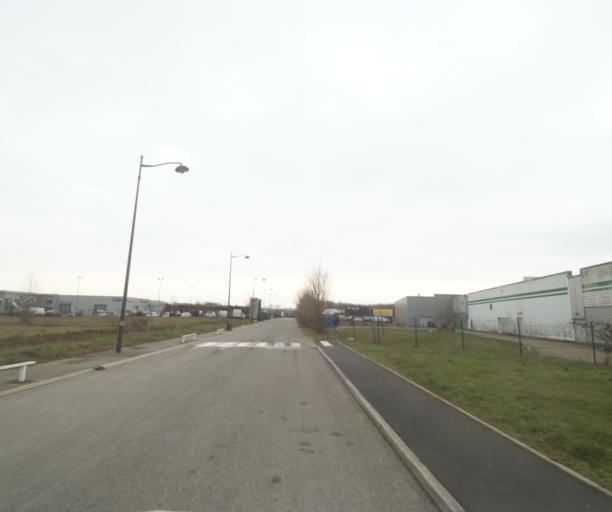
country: FR
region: Champagne-Ardenne
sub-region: Departement de la Haute-Marne
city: Saint-Dizier
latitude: 48.6262
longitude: 4.9673
